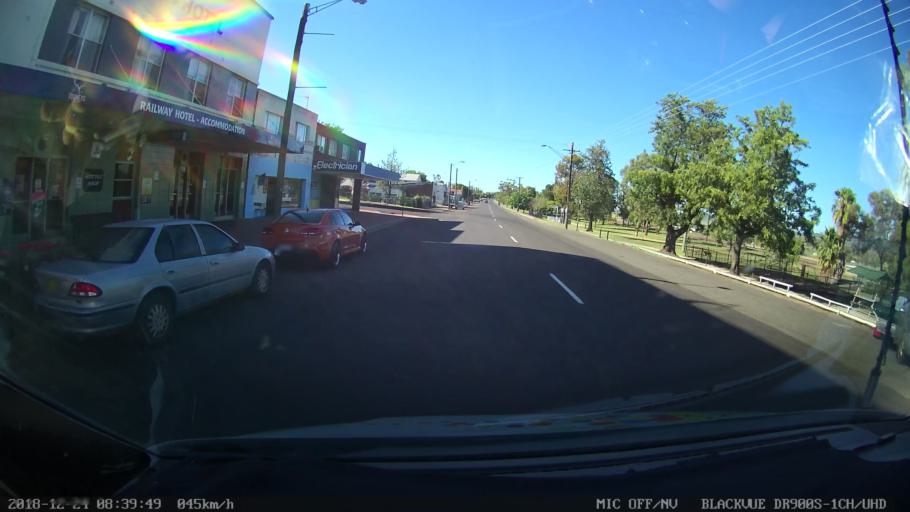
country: AU
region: New South Wales
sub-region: Liverpool Plains
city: Quirindi
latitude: -31.3506
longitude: 150.6471
